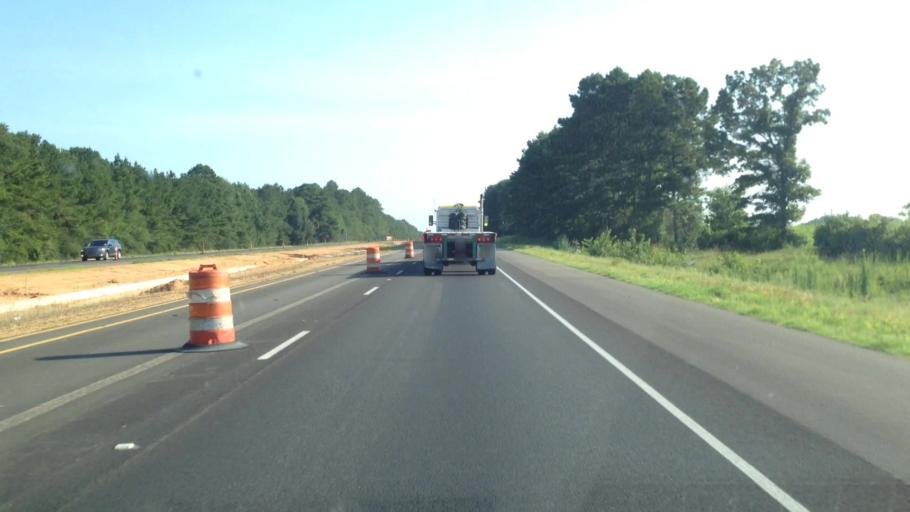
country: US
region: Mississippi
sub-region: Pike County
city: McComb
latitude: 31.1962
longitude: -90.4841
